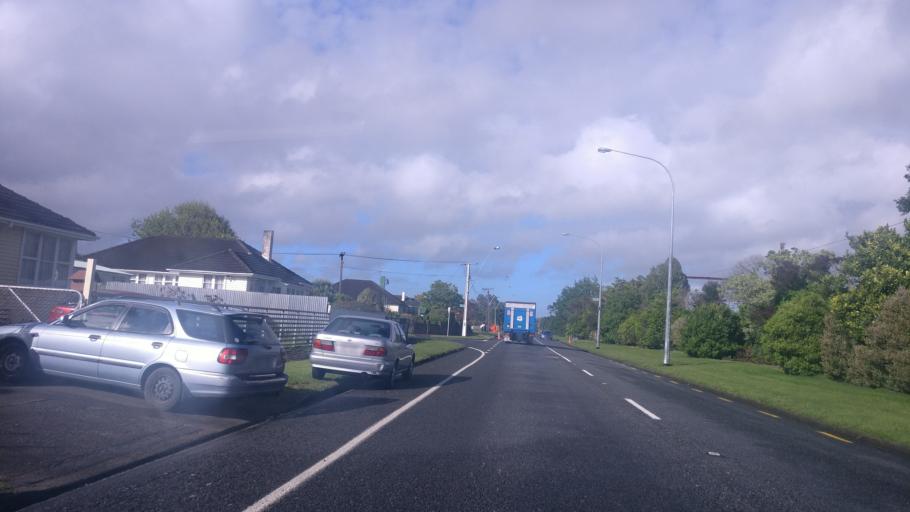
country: NZ
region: Wellington
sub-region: Lower Hutt City
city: Lower Hutt
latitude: -41.2035
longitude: 174.9372
